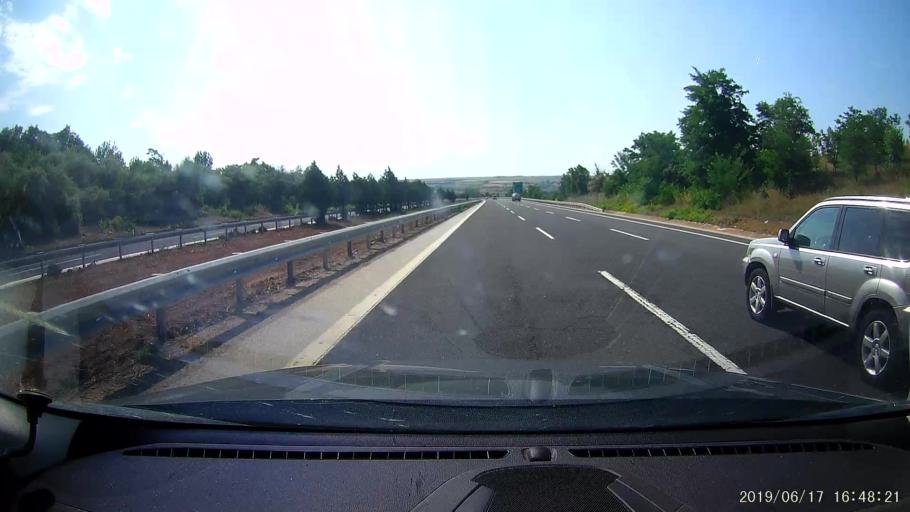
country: TR
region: Kirklareli
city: Babaeski
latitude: 41.5055
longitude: 27.1446
